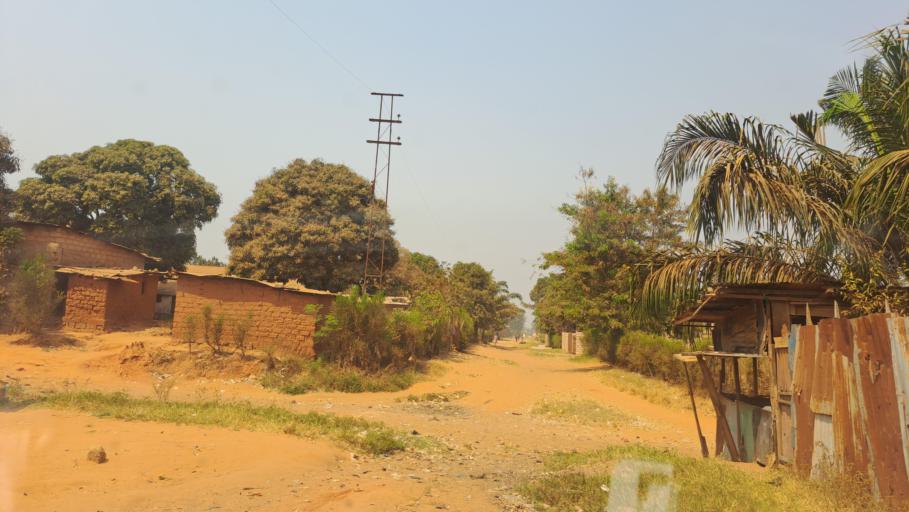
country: CD
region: Kasai-Oriental
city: Mbuji-Mayi
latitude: -6.1246
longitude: 23.6108
